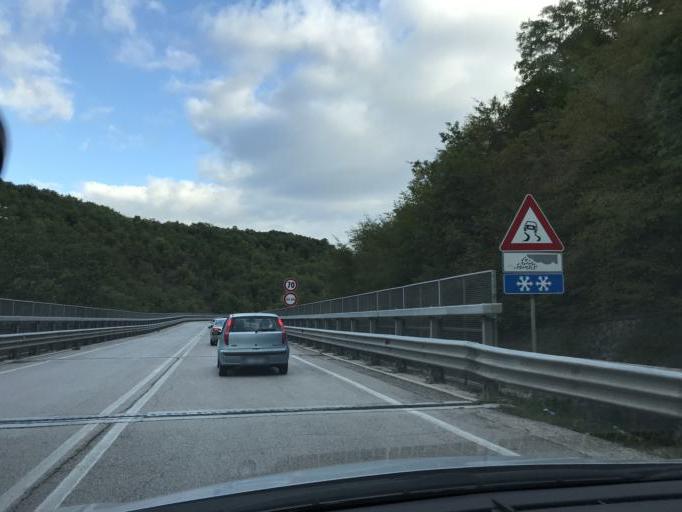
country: IT
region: Umbria
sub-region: Provincia di Perugia
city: Spoleto
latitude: 42.6749
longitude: 12.7262
